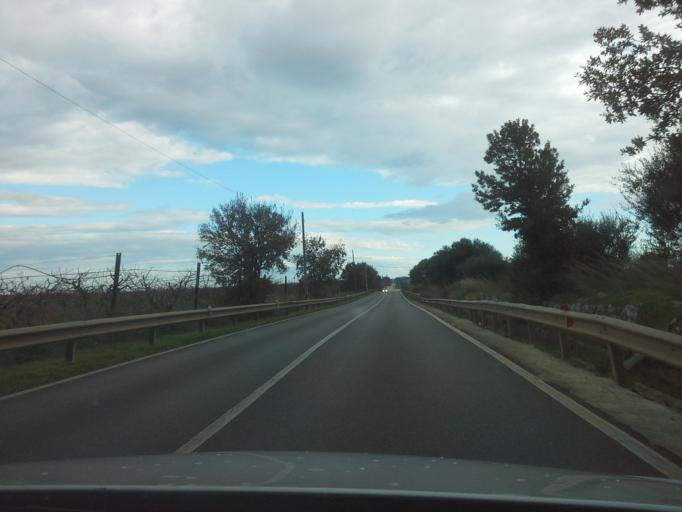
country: IT
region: Apulia
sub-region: Provincia di Bari
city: Turi
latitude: 40.9283
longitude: 16.9915
